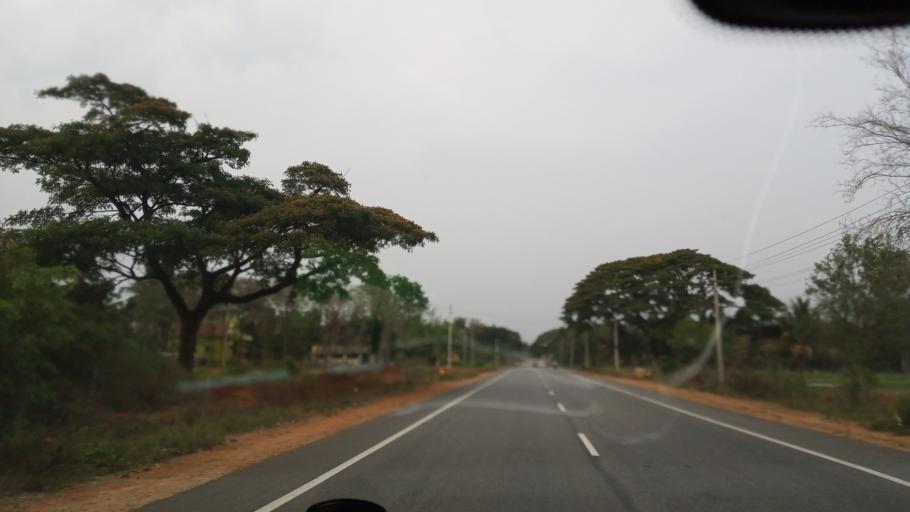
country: IN
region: Karnataka
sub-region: Mandya
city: Nagamangala
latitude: 12.7637
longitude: 76.7359
